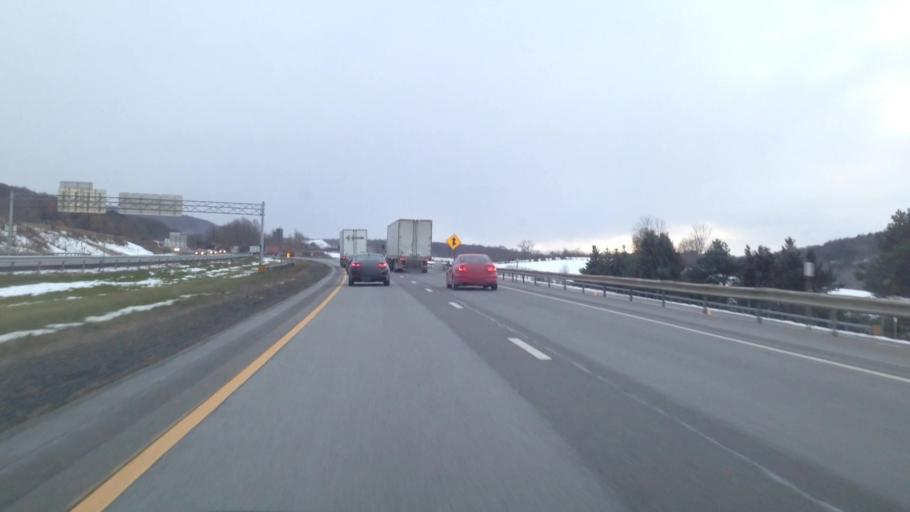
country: US
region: New York
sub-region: Herkimer County
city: Little Falls
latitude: 43.0160
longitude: -74.8224
